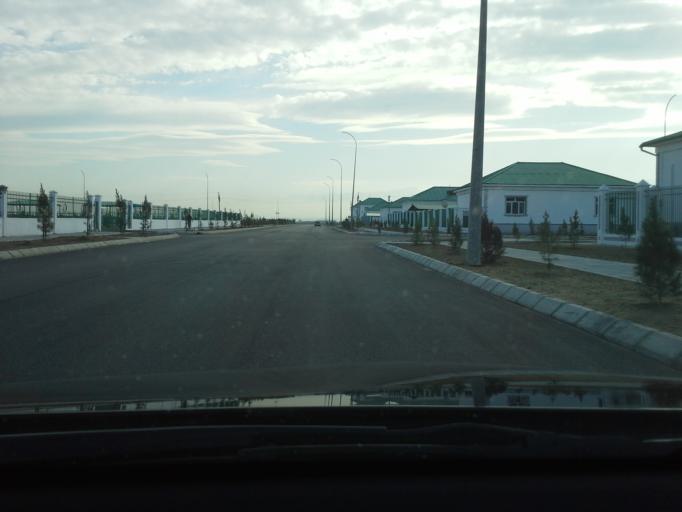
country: TM
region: Ahal
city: Abadan
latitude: 38.0963
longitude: 58.3084
